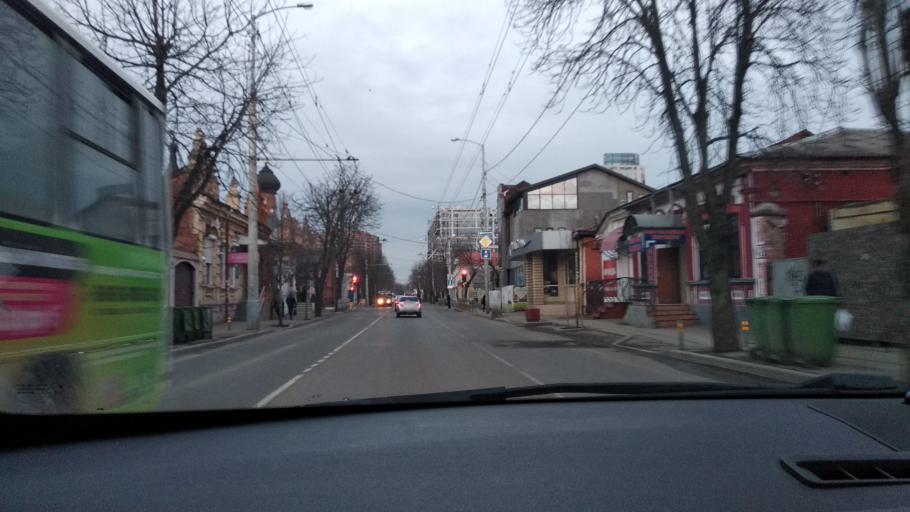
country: RU
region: Krasnodarskiy
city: Krasnodar
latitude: 45.0327
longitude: 38.9688
